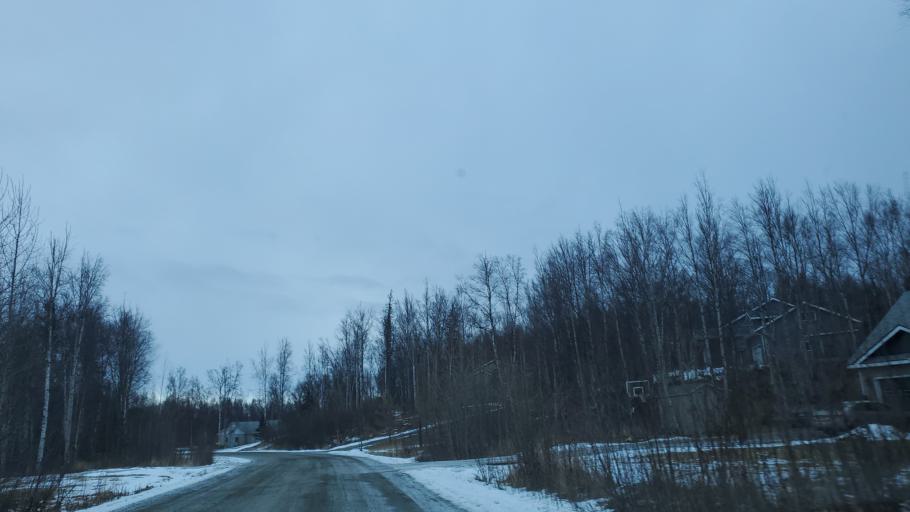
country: US
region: Alaska
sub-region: Matanuska-Susitna Borough
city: Farm Loop
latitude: 61.6536
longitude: -149.2215
